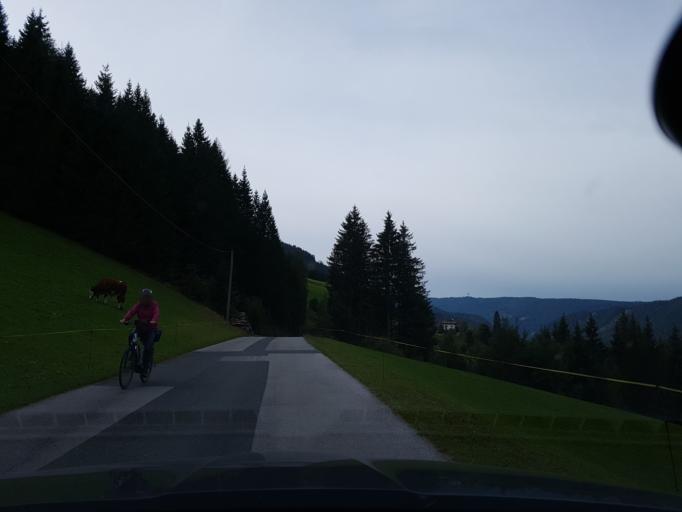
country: AT
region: Salzburg
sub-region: Politischer Bezirk Sankt Johann im Pongau
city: Forstau
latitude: 47.3590
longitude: 13.5643
